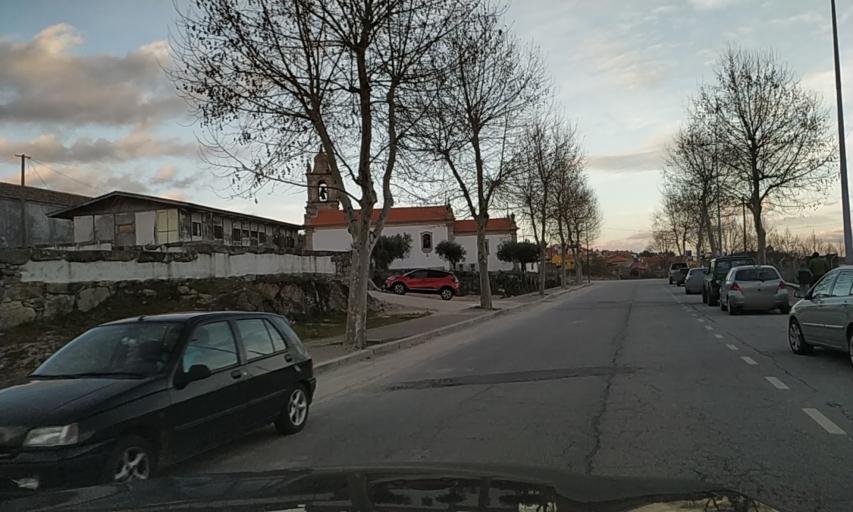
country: PT
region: Braganca
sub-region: Carrazeda de Ansiaes
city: Carrazeda de Anciaes
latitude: 41.2424
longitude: -7.3020
